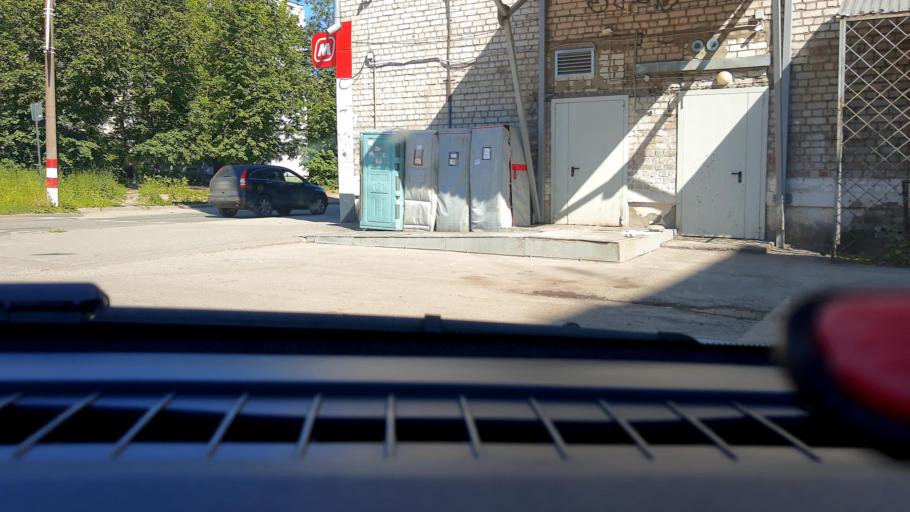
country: RU
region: Nizjnij Novgorod
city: Gidrotorf
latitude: 56.5178
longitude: 43.5555
